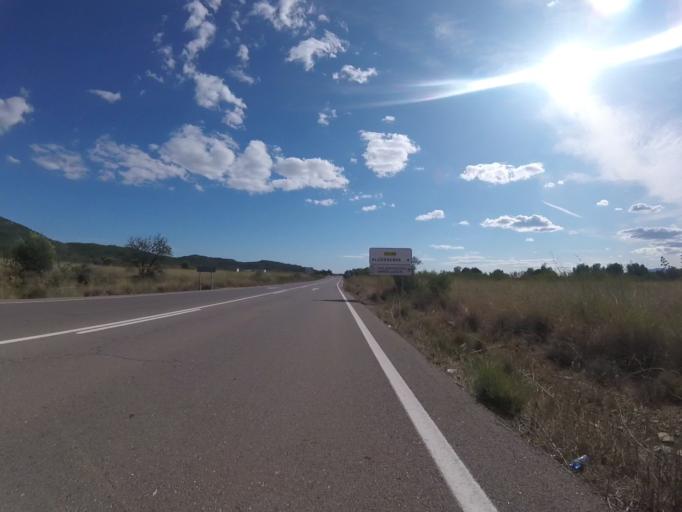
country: ES
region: Valencia
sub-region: Provincia de Castello
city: Alcala de Xivert
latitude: 40.2650
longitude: 0.2422
